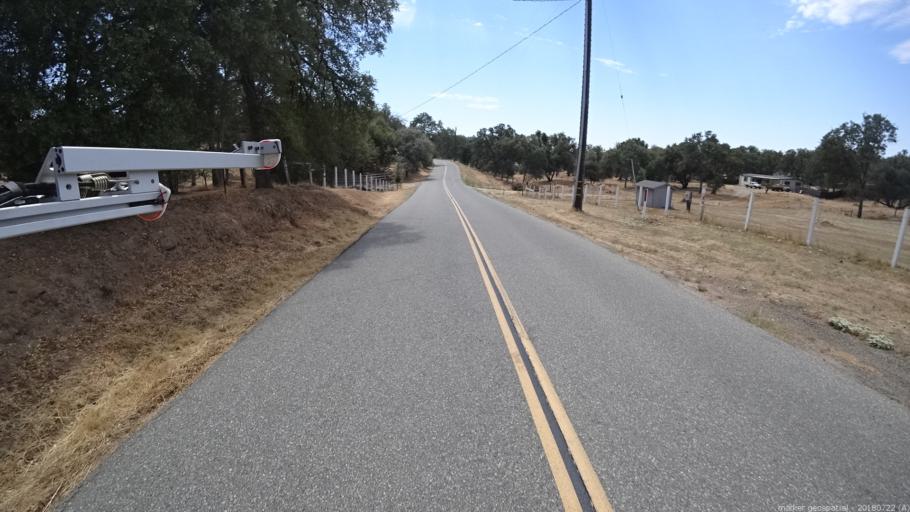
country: US
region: California
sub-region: Madera County
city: Coarsegold
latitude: 37.2754
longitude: -119.7430
